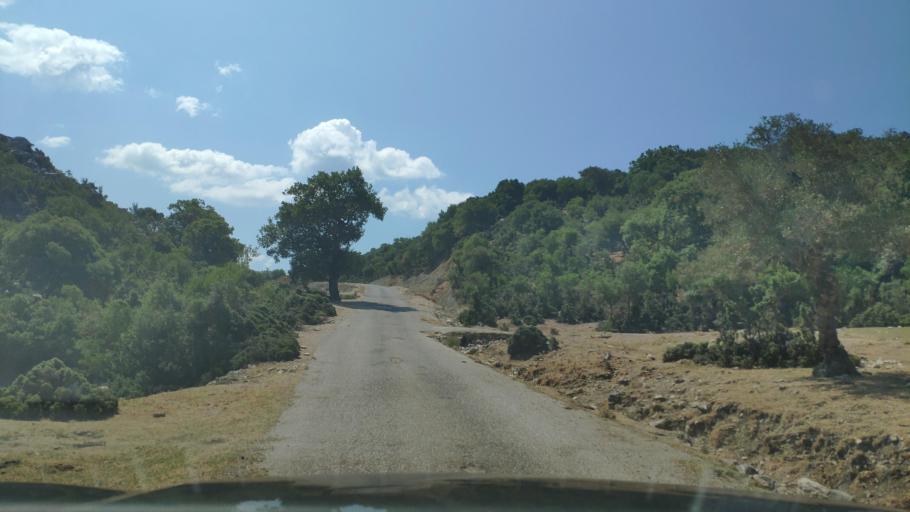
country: GR
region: West Greece
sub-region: Nomos Aitolias kai Akarnanias
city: Monastirakion
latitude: 38.8237
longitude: 20.9283
